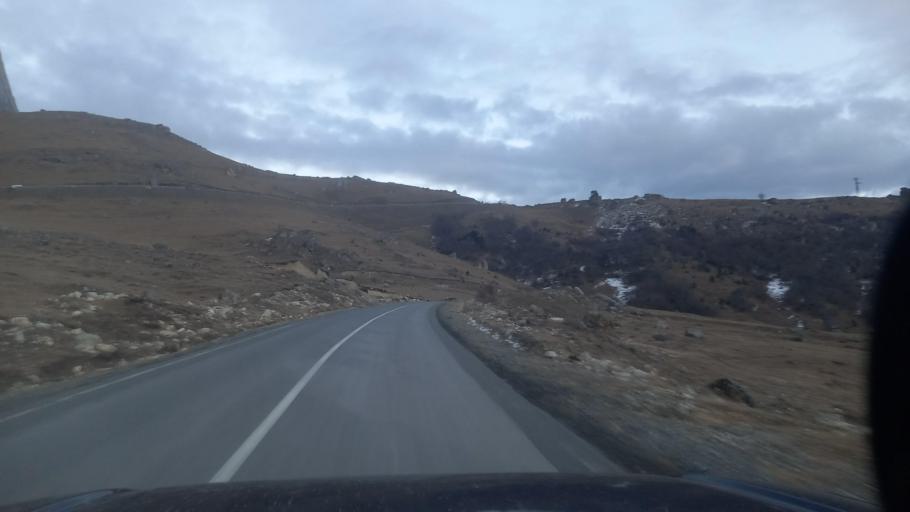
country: RU
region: Ingushetiya
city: Dzhayrakh
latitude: 42.8212
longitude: 44.8229
